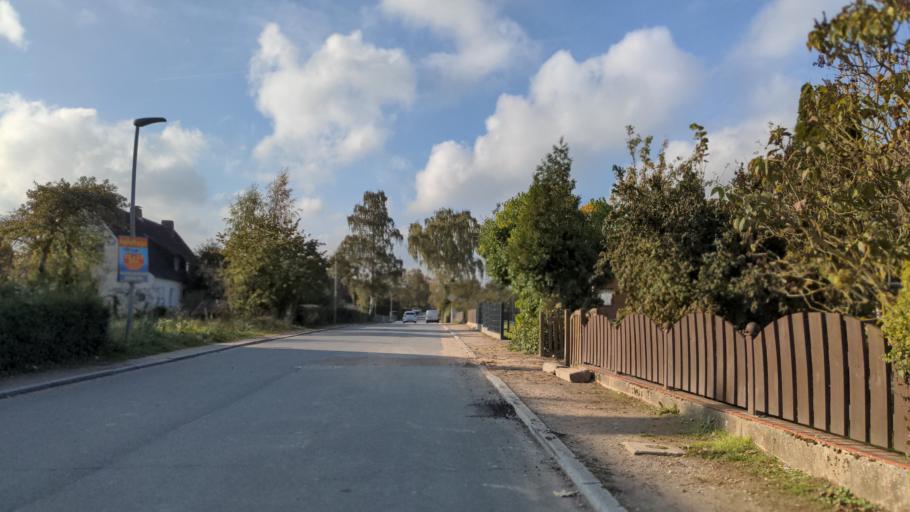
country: DE
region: Schleswig-Holstein
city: Beschendorf
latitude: 54.2074
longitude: 10.8742
